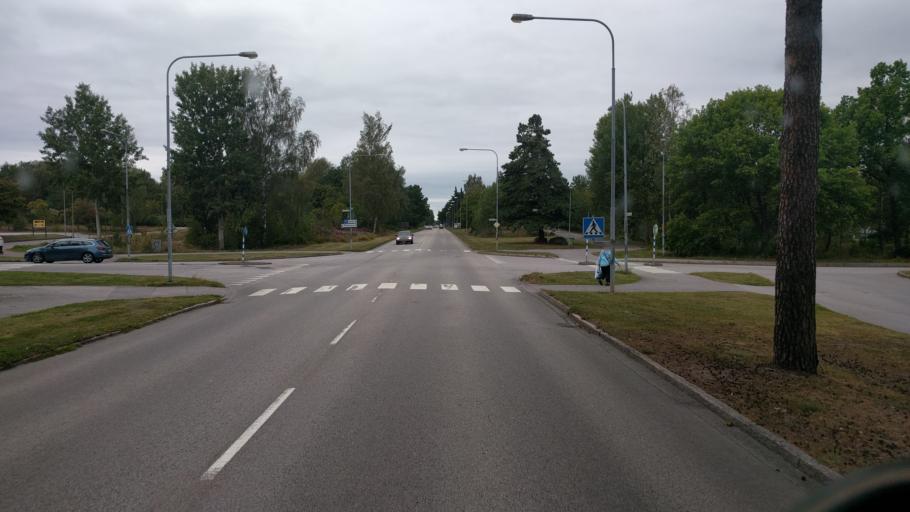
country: SE
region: Kalmar
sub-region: Vasterviks Kommun
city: Vaestervik
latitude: 57.7459
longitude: 16.6460
